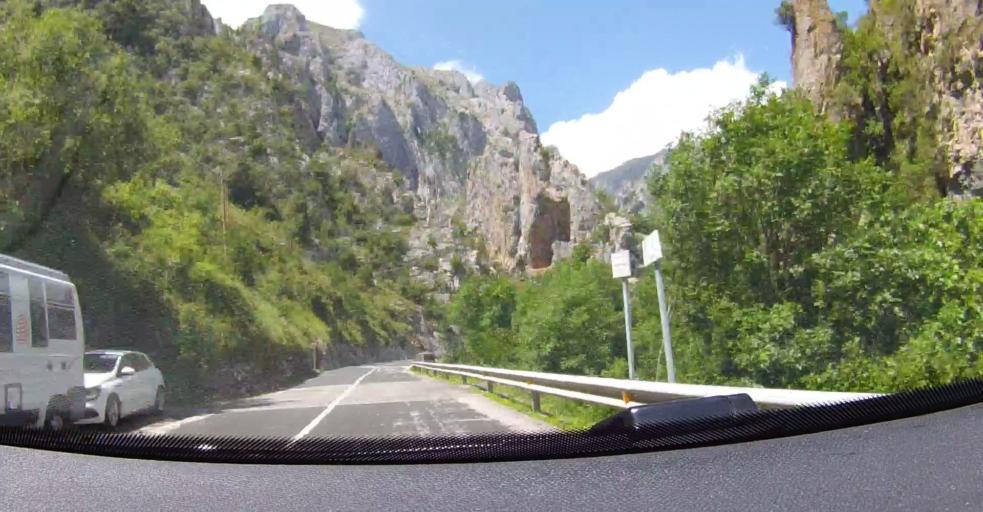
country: ES
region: Cantabria
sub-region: Provincia de Cantabria
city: Tresviso
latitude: 43.2662
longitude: -4.6304
